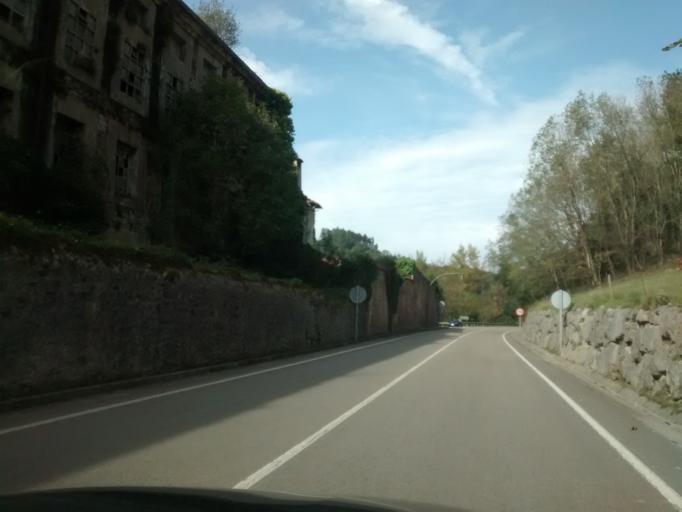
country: ES
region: Cantabria
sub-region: Provincia de Cantabria
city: Entrambasaguas
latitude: 43.3612
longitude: -3.7122
